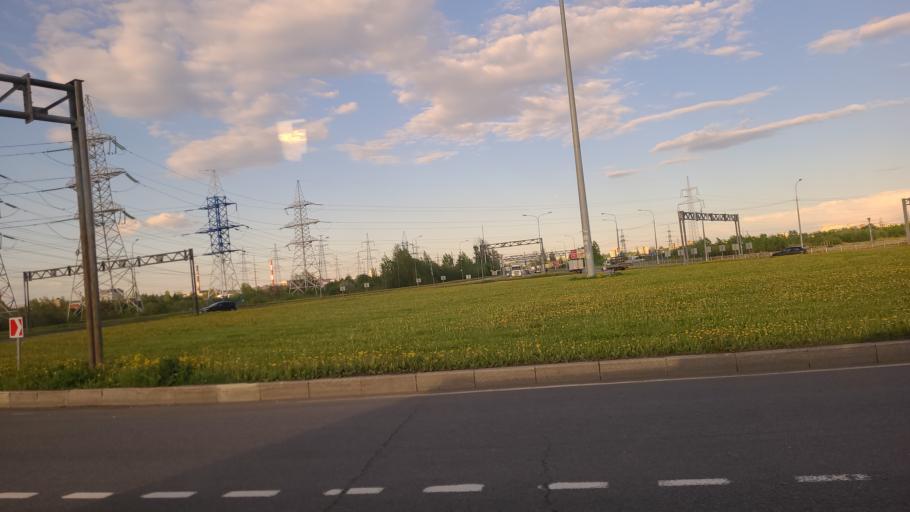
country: RU
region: St.-Petersburg
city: Metallostroy
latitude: 59.7486
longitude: 30.5314
